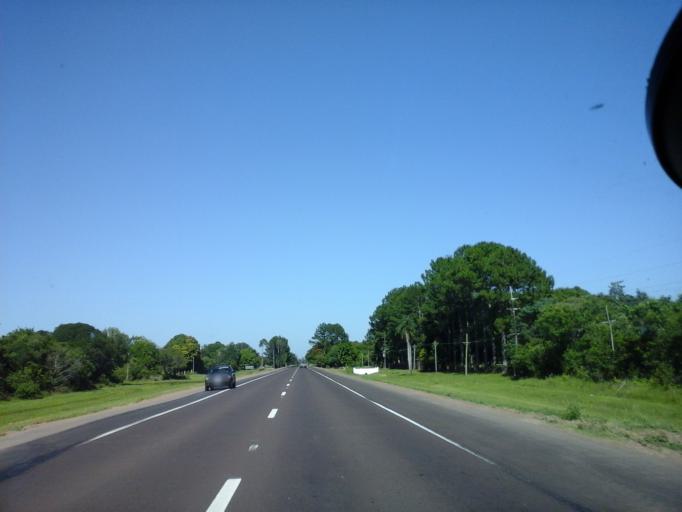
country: AR
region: Corrientes
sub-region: Departamento de San Cosme
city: San Cosme
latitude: -27.3683
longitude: -58.4155
